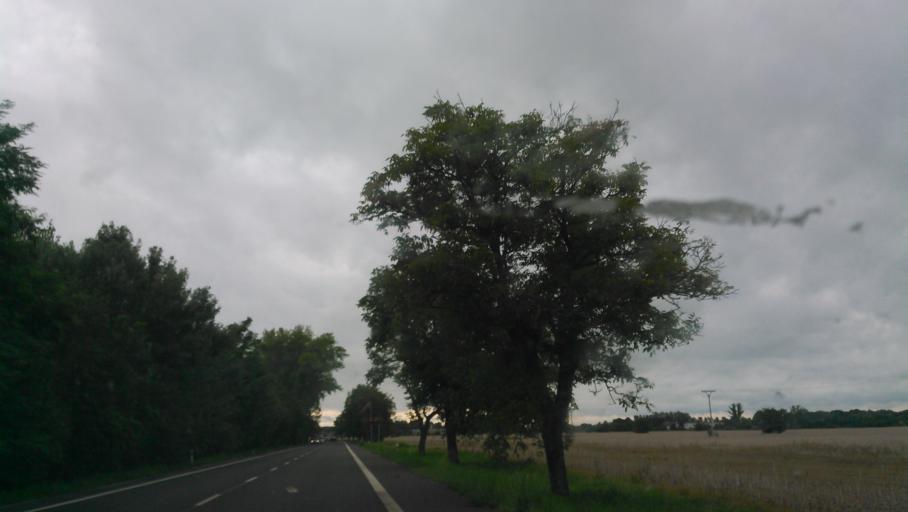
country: SK
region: Trnavsky
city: Dunajska Streda
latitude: 47.9597
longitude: 17.6969
